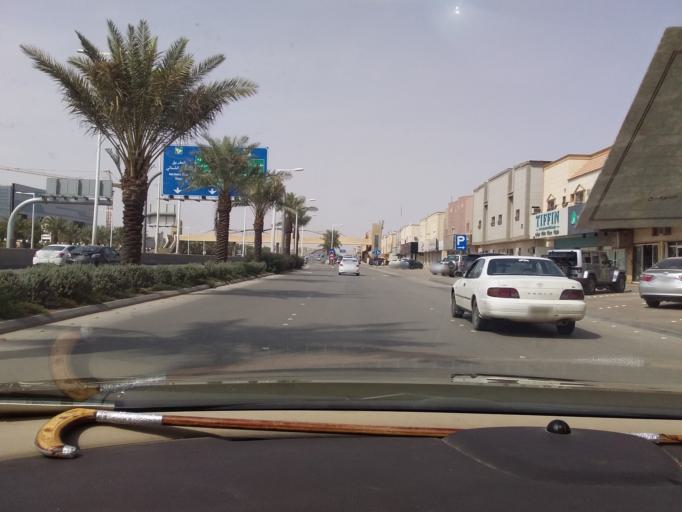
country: SA
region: Ar Riyad
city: Riyadh
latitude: 24.7383
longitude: 46.7064
